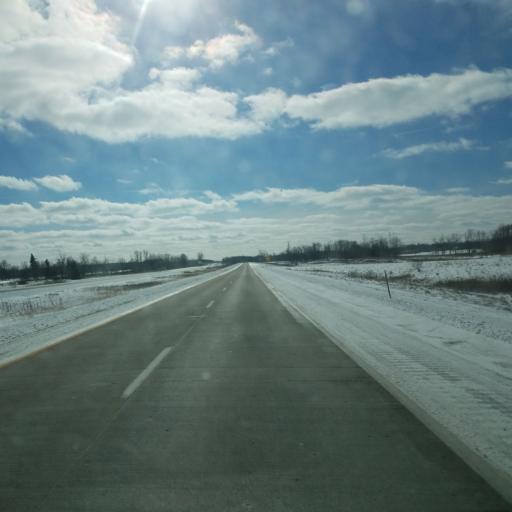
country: US
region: Michigan
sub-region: Clinton County
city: Saint Johns
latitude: 42.9259
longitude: -84.5190
